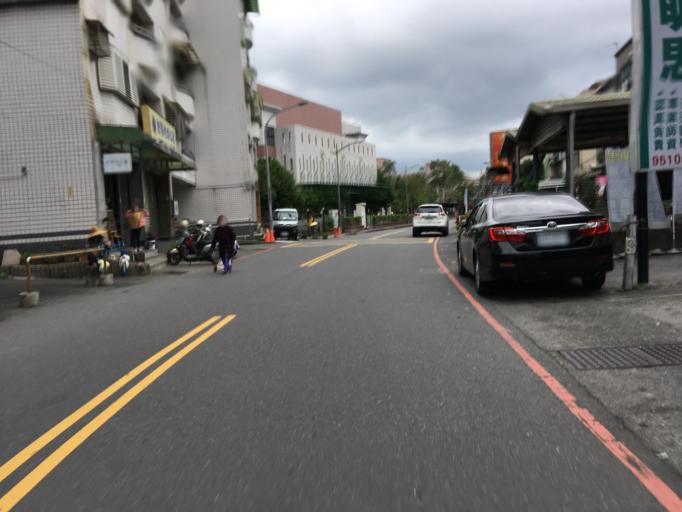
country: TW
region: Taiwan
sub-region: Yilan
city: Yilan
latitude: 24.6737
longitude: 121.7592
